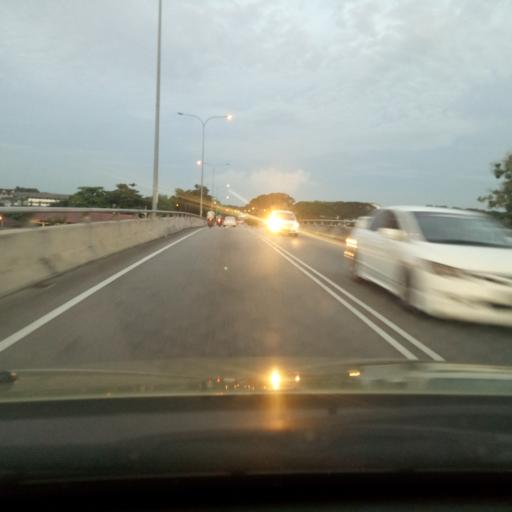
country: MY
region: Kedah
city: Alor Setar
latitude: 6.1170
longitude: 100.3717
